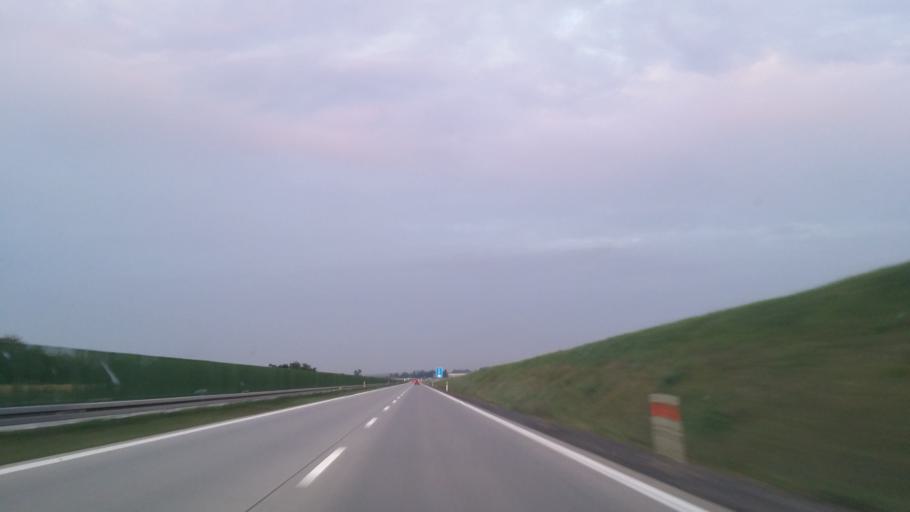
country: PL
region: Lower Silesian Voivodeship
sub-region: Powiat sredzki
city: Udanin
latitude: 51.1155
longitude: 16.3839
